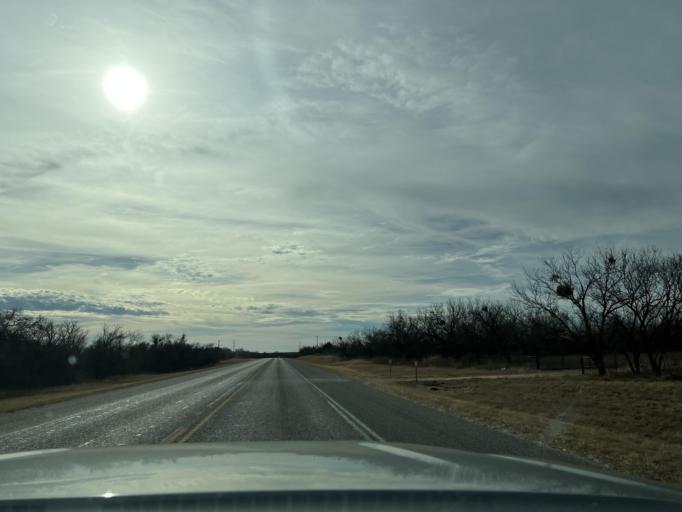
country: US
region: Texas
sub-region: Jones County
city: Stamford
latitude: 32.7612
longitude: -99.6020
